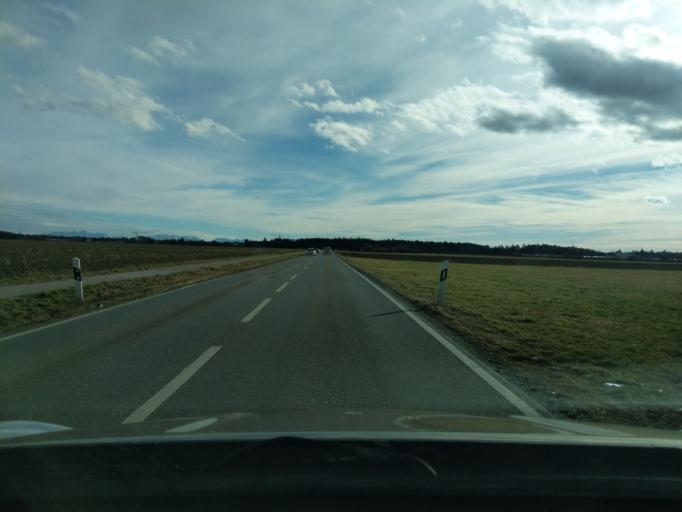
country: DE
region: Bavaria
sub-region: Upper Bavaria
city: Vaterstetten
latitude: 48.1308
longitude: 11.7665
